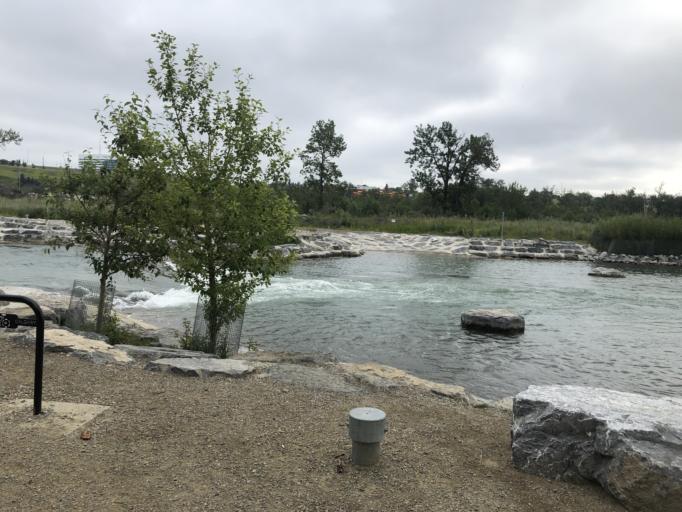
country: CA
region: Alberta
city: Calgary
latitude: 51.0406
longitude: -114.0120
